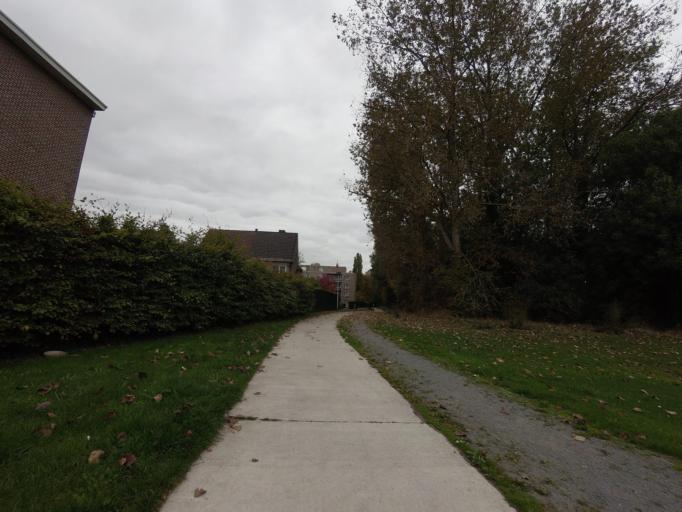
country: BE
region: Flanders
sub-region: Provincie Antwerpen
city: Antwerpen
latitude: 51.2516
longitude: 4.4296
